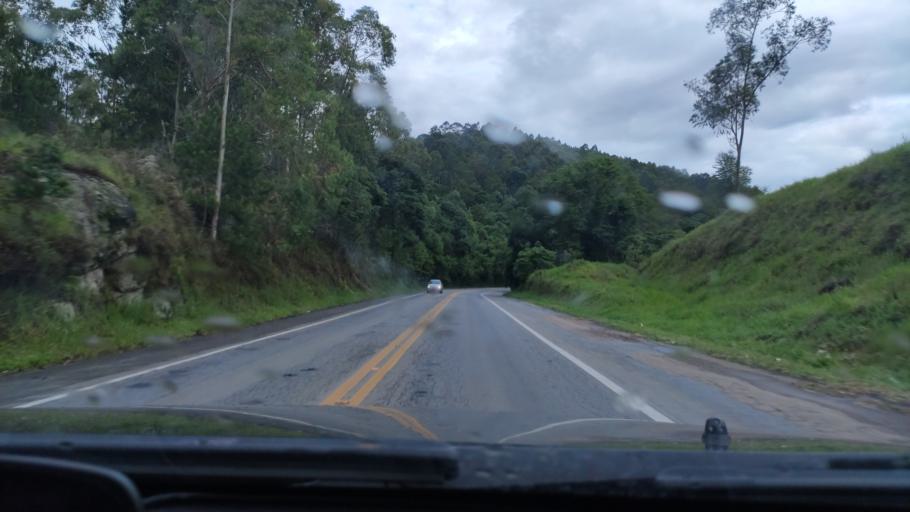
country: BR
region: Sao Paulo
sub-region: Braganca Paulista
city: Braganca Paulista
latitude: -22.8239
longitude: -46.5548
